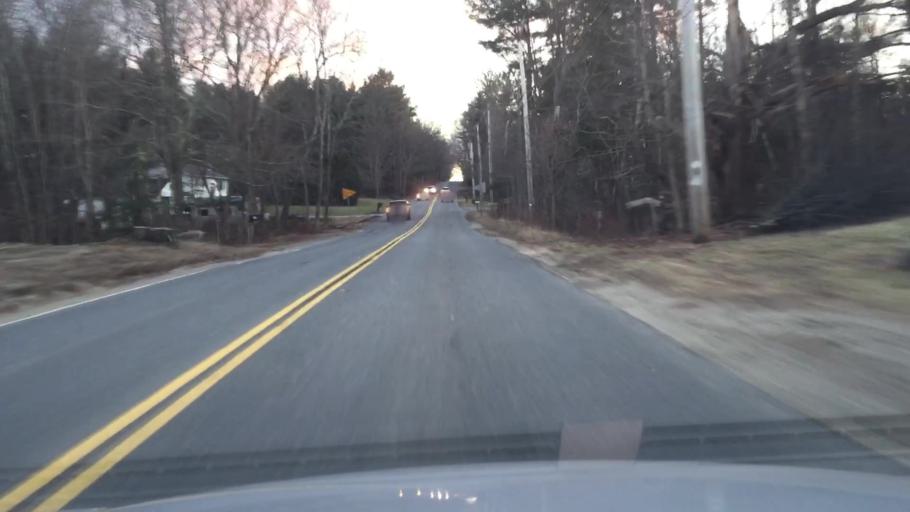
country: US
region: Massachusetts
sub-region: Worcester County
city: Sterling
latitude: 42.4143
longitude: -71.8017
